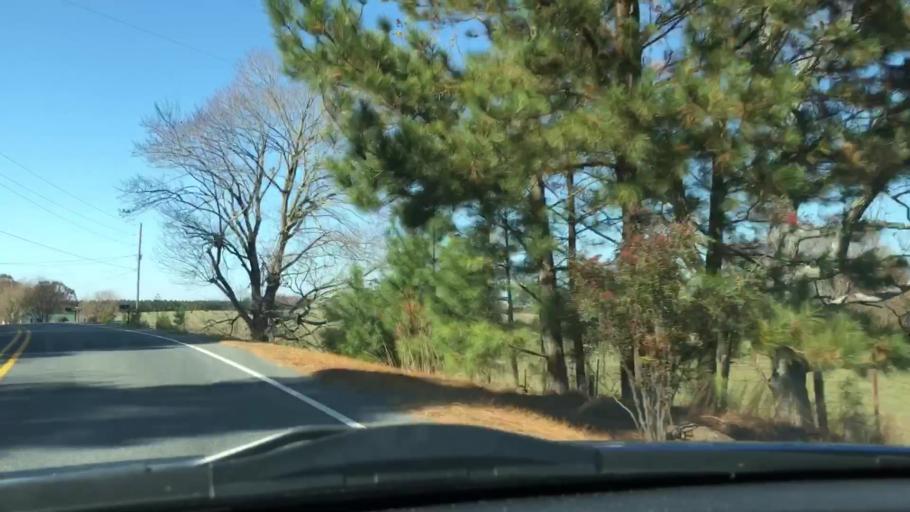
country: US
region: North Carolina
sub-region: Randolph County
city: Asheboro
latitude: 35.6828
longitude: -79.8515
